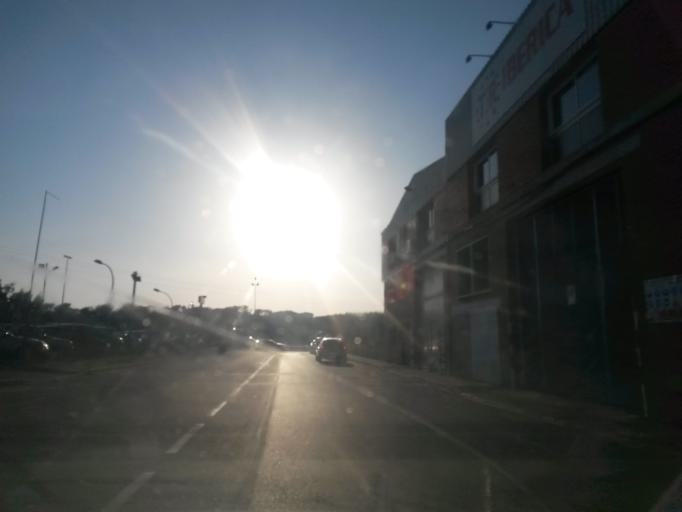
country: ES
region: Catalonia
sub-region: Provincia de Girona
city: Fornells de la Selva
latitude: 41.9315
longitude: 2.7963
